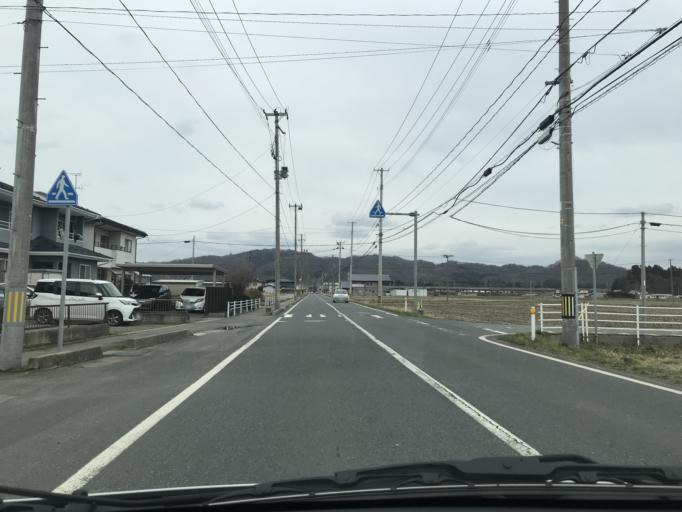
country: JP
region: Iwate
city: Kitakami
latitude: 39.2723
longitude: 141.1077
